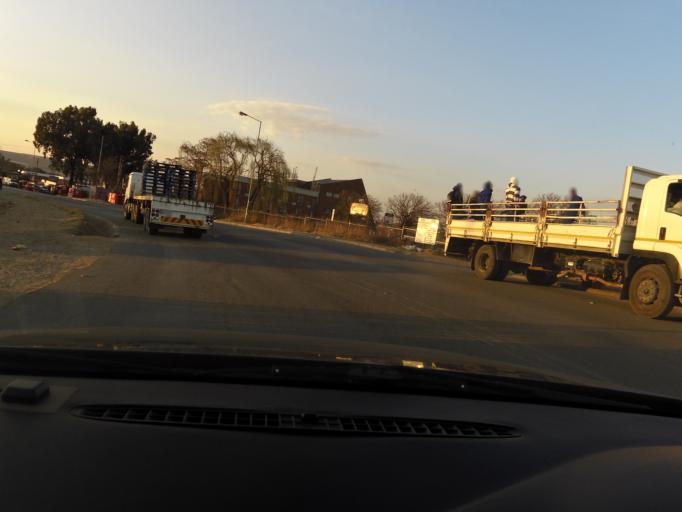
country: LS
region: Maseru
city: Maseru
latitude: -29.3146
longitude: 27.5107
